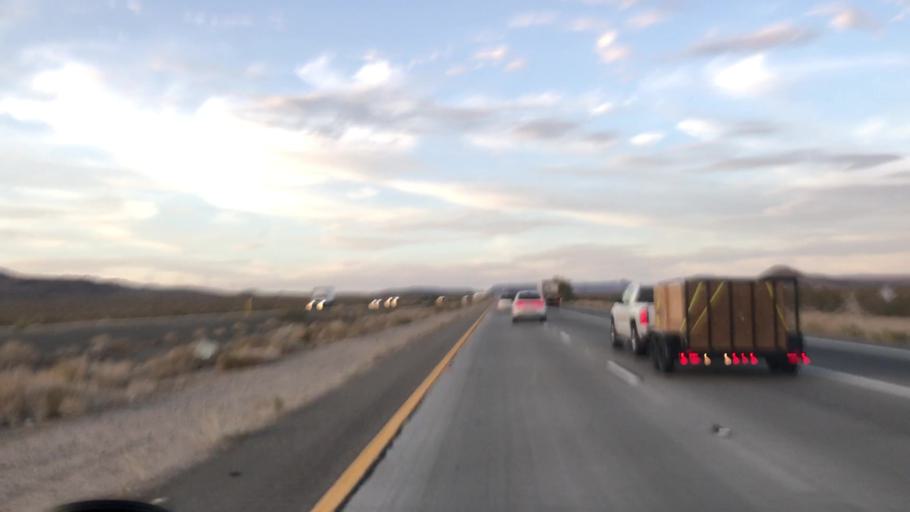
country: US
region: Nevada
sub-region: Clark County
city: Sandy Valley
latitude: 35.3403
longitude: -115.9563
